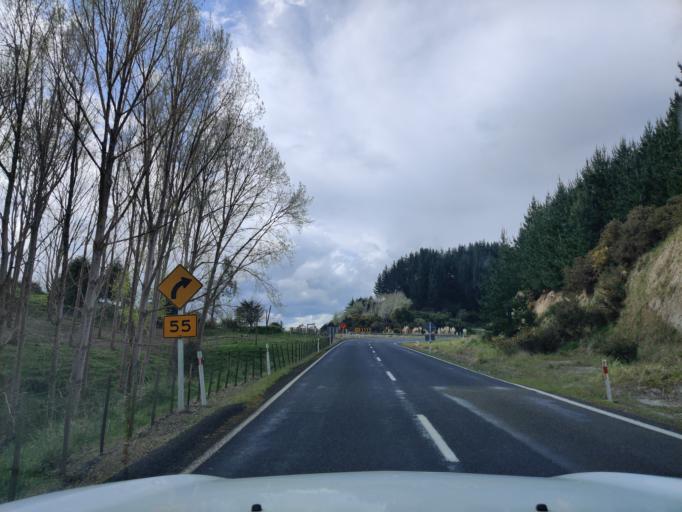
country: NZ
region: Manawatu-Wanganui
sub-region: Wanganui District
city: Wanganui
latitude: -39.7995
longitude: 175.1970
